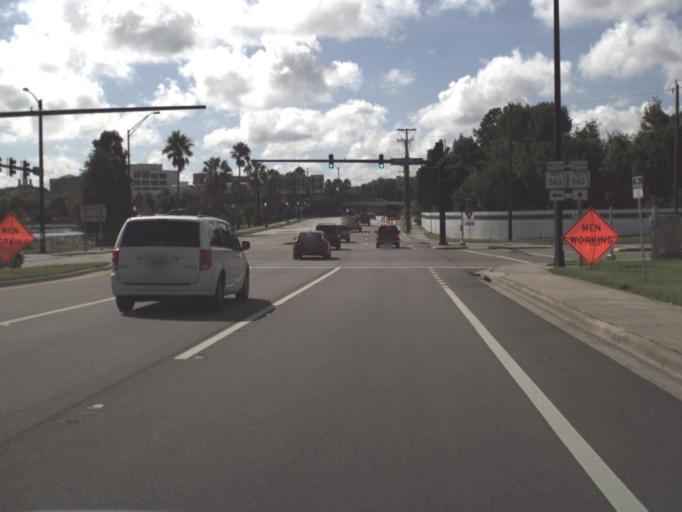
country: US
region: Florida
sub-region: Polk County
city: Lakeland
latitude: 28.0473
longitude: -81.9632
